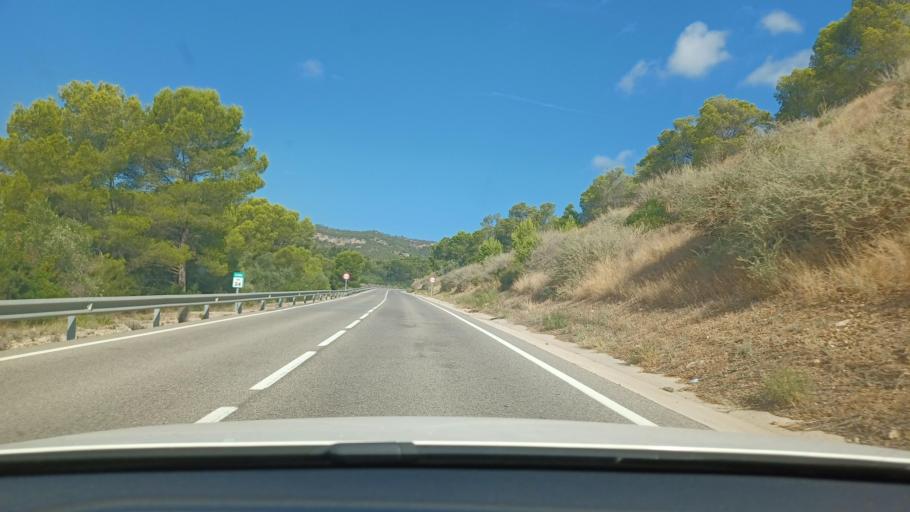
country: ES
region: Catalonia
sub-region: Provincia de Tarragona
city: Tivenys
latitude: 40.9365
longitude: 0.4709
